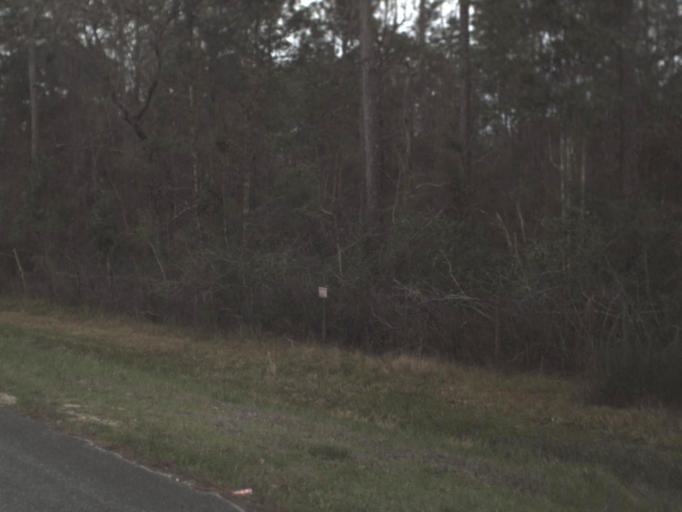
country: US
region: Florida
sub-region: Wakulla County
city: Crawfordville
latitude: 30.2821
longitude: -84.3924
